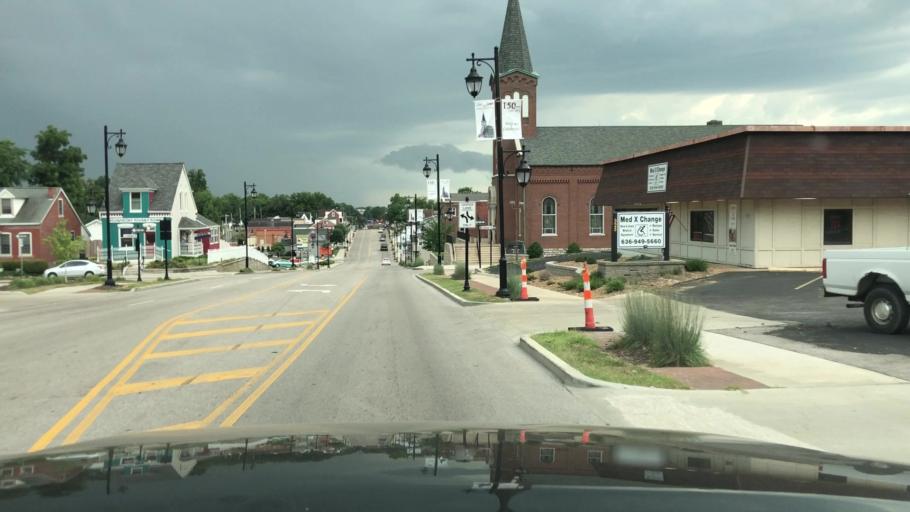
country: US
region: Missouri
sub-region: Saint Charles County
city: Saint Charles
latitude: 38.7806
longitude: -90.4872
